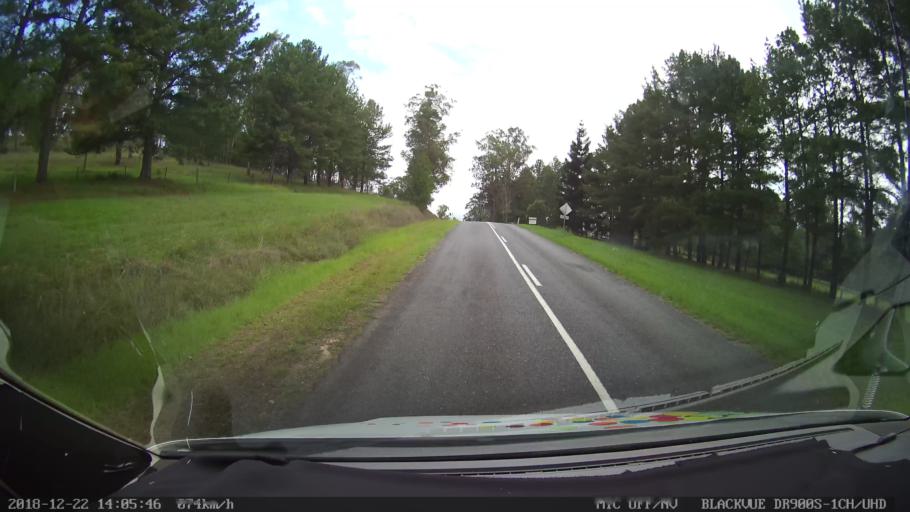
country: AU
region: New South Wales
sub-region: Clarence Valley
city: Coutts Crossing
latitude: -29.9486
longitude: 152.7288
